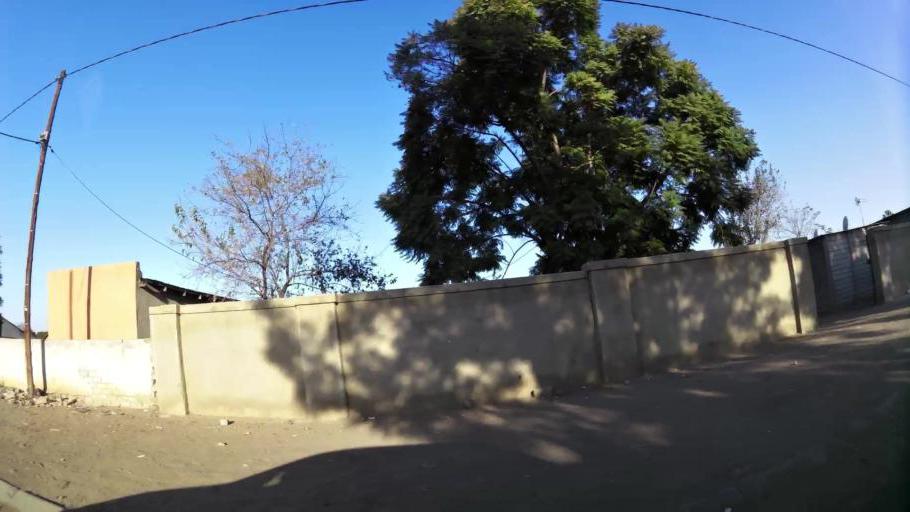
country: ZA
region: North-West
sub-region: Bojanala Platinum District Municipality
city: Rustenburg
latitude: -25.6414
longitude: 27.2180
